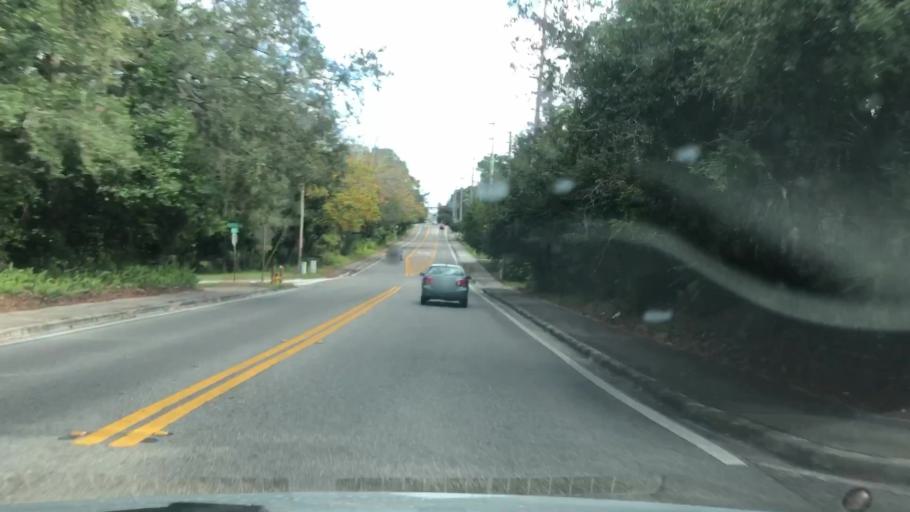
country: US
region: Florida
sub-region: Seminole County
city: Altamonte Springs
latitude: 28.6837
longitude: -81.3771
